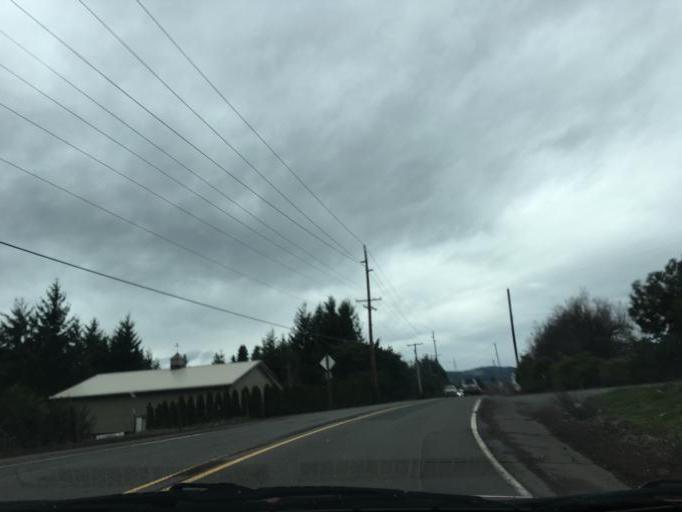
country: US
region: Oregon
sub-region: Hood River County
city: Hood River
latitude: 45.6787
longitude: -121.5293
